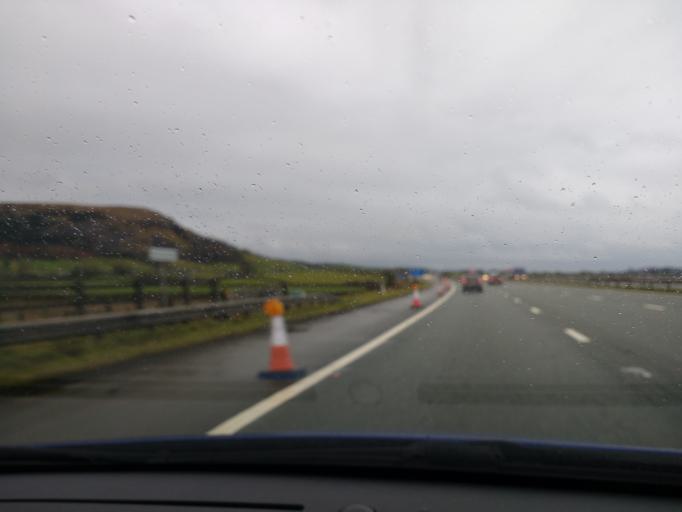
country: GB
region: England
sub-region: Cumbria
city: Milnthorpe
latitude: 54.2305
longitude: -2.7208
